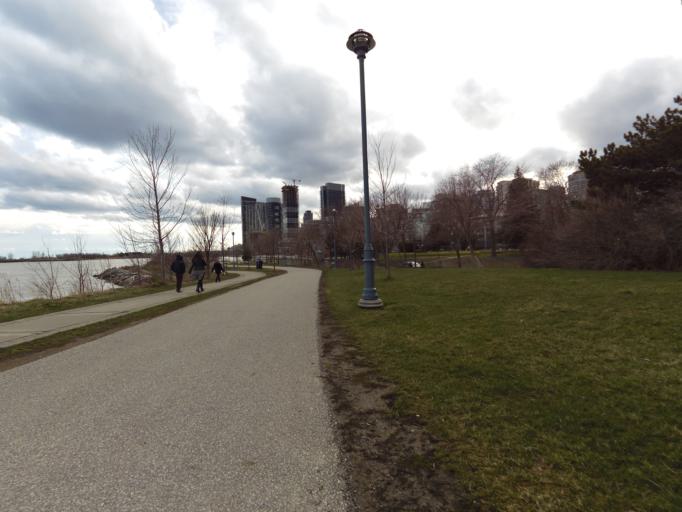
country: CA
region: Ontario
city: Toronto
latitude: 43.6309
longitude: -79.4721
